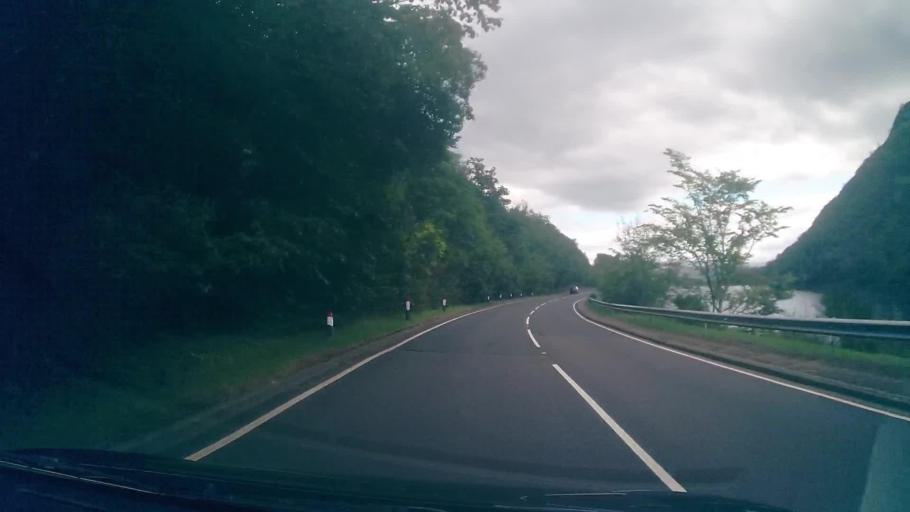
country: GB
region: Scotland
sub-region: Argyll and Bute
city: Oban
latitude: 56.3976
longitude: -5.1329
